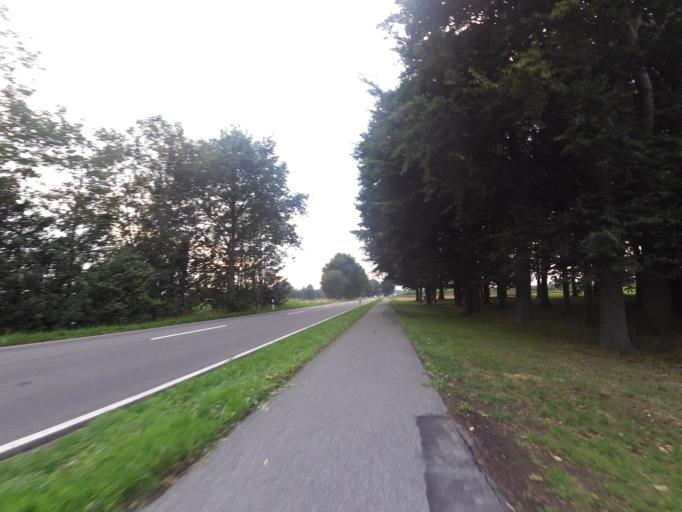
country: NL
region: Gelderland
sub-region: Oude IJsselstreek
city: Gendringen
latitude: 51.8581
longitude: 6.4030
